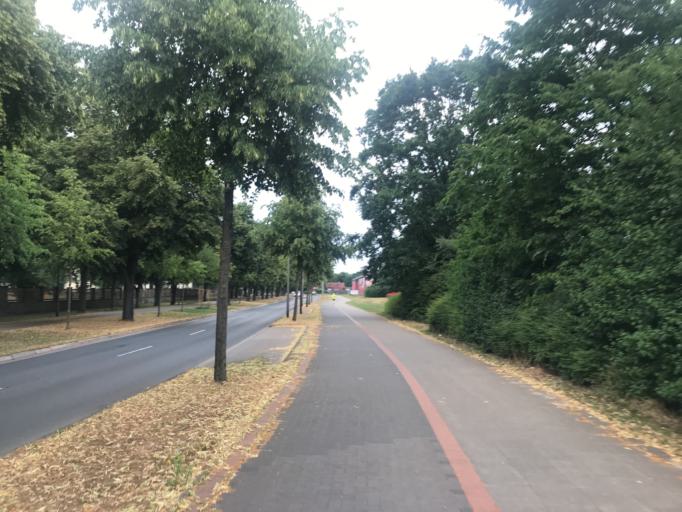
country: DE
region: Lower Saxony
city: Langenhagen
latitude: 52.4169
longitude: 9.7935
